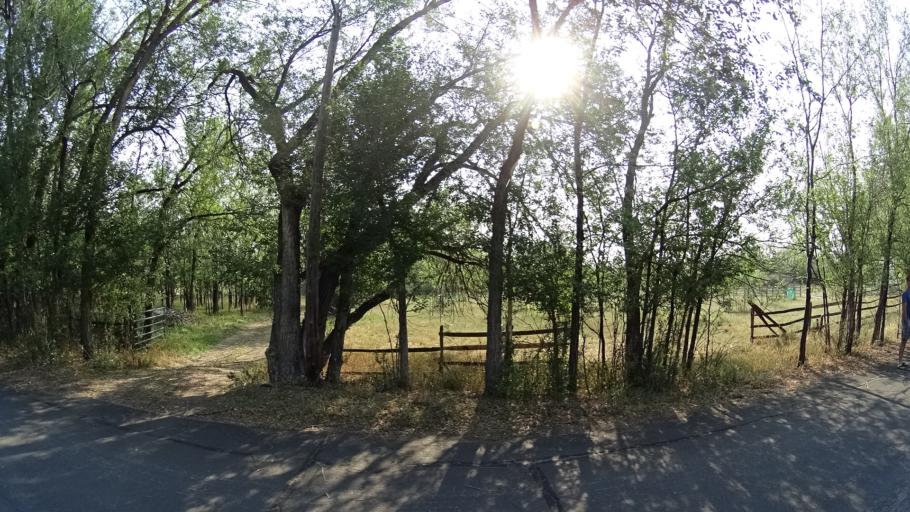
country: US
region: Colorado
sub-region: El Paso County
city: Colorado Springs
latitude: 38.8017
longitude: -104.8502
